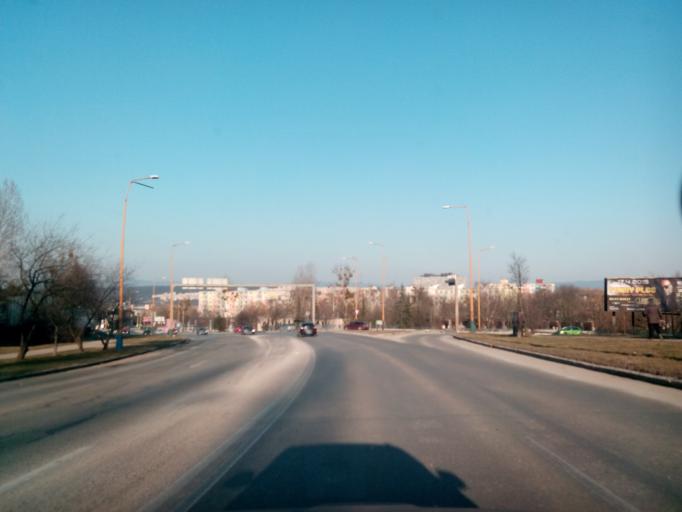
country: SK
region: Kosicky
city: Kosice
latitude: 48.7213
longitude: 21.2252
